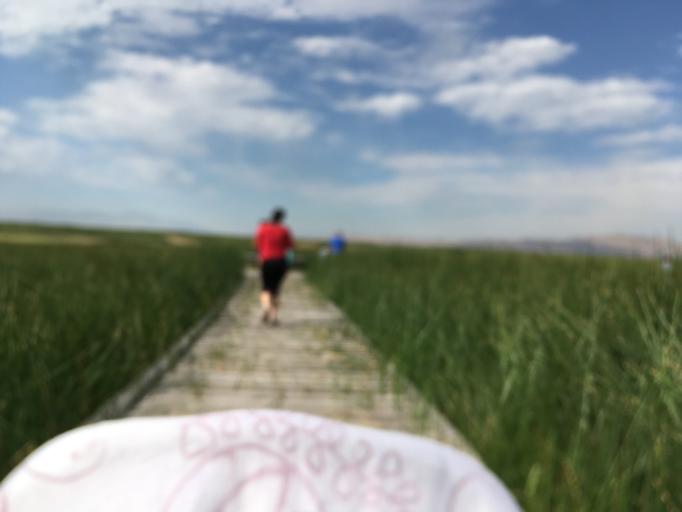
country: US
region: Utah
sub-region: Davis County
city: Layton
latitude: 41.0362
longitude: -112.0260
